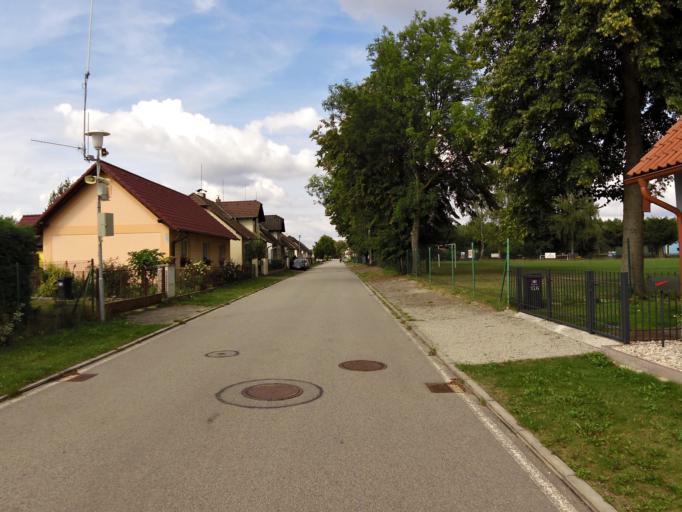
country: CZ
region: Jihocesky
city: Suchdol nad Luznici
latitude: 48.9092
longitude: 14.9152
